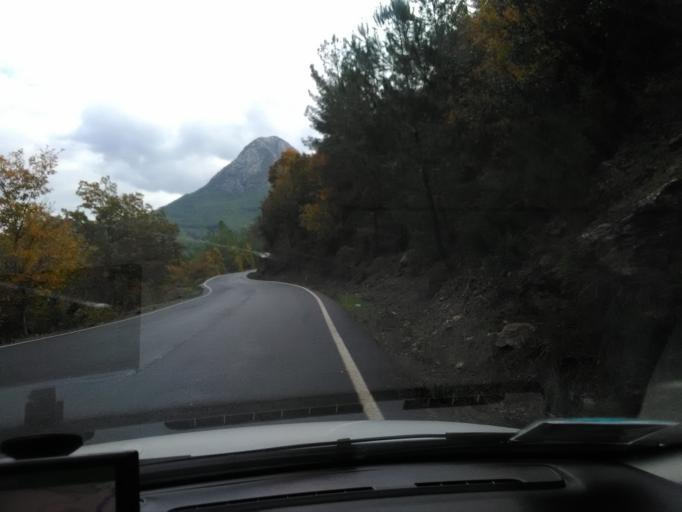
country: TR
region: Antalya
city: Gazipasa
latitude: 36.2506
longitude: 32.4043
